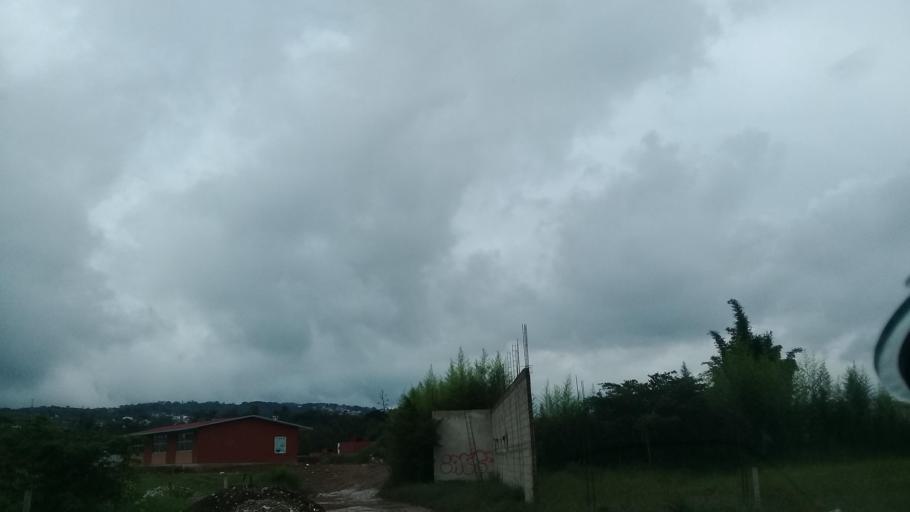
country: MX
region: Veracruz
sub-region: Emiliano Zapata
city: Las Trancas
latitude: 19.4974
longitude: -96.8671
